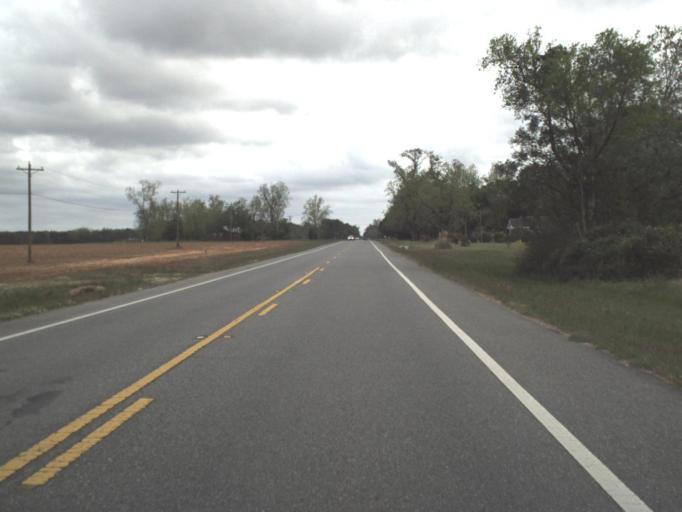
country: US
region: Florida
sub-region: Santa Rosa County
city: Point Baker
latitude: 30.7736
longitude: -87.0419
